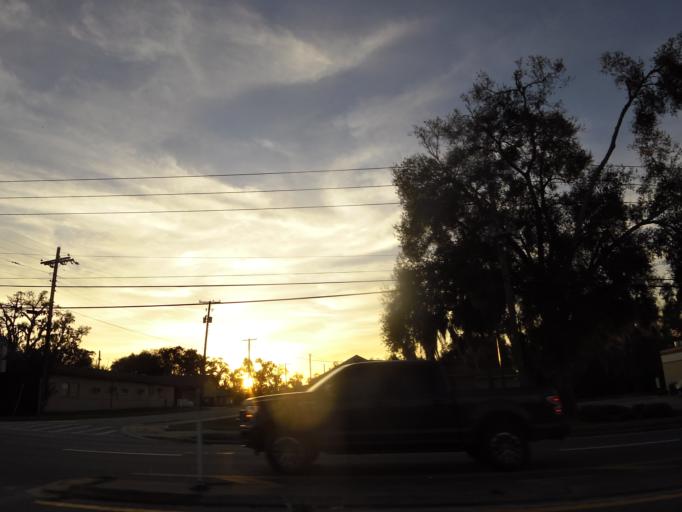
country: US
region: Florida
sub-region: Volusia County
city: North DeLand
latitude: 29.0519
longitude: -81.3042
